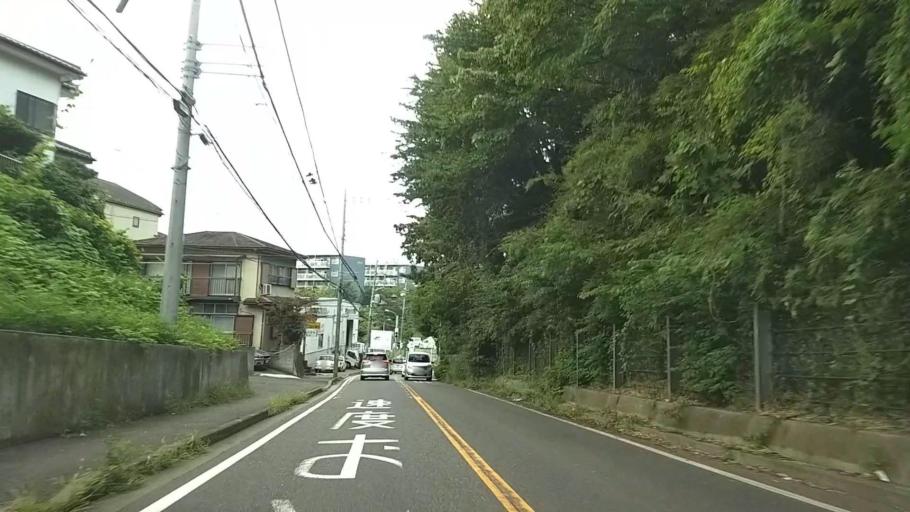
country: JP
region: Kanagawa
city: Yokohama
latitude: 35.4966
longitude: 139.5661
